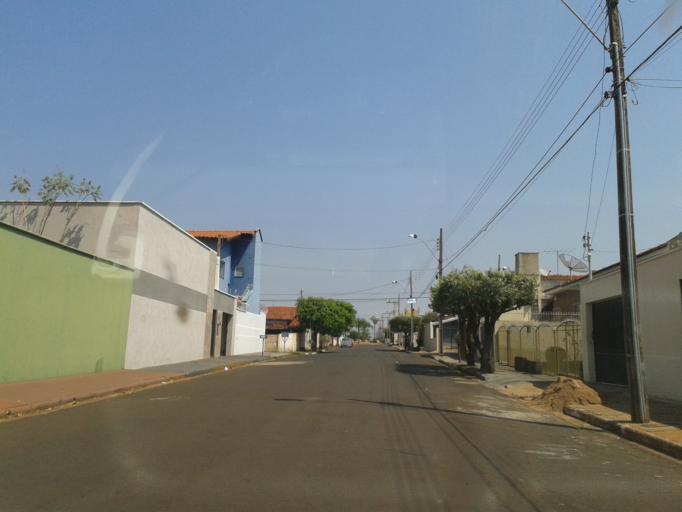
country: BR
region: Minas Gerais
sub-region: Ituiutaba
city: Ituiutaba
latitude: -18.9763
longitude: -49.4742
